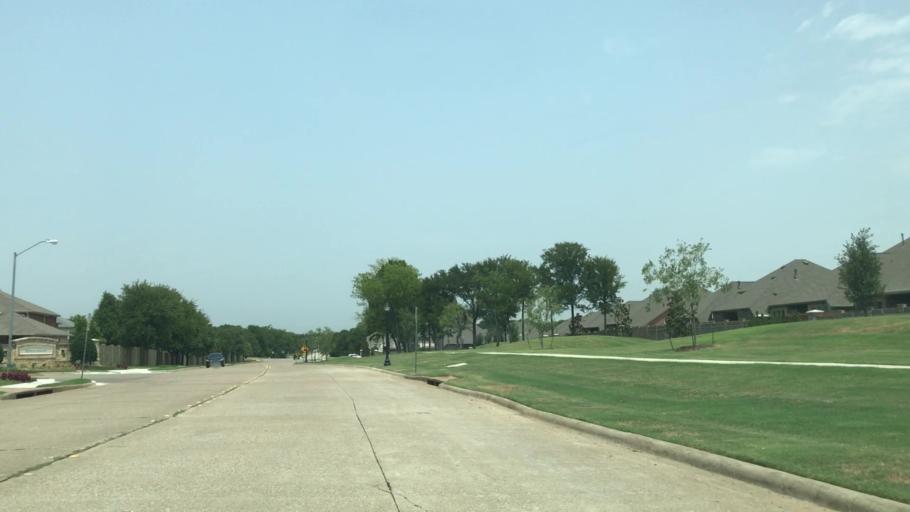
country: US
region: Texas
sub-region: Tarrant County
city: Euless
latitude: 32.8438
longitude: -97.0725
